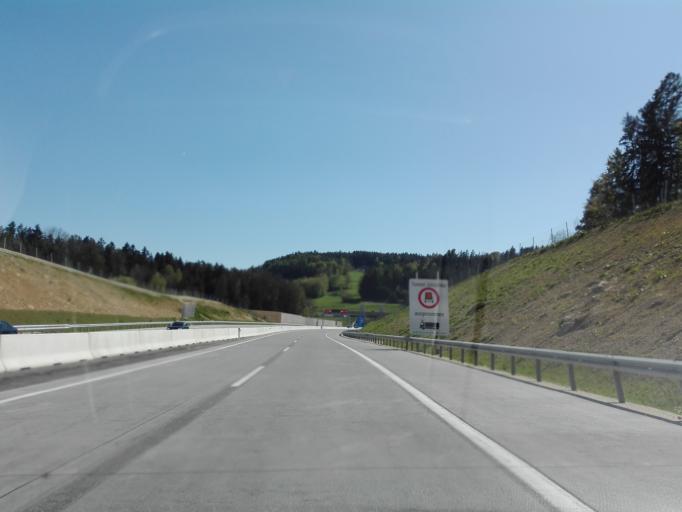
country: AT
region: Upper Austria
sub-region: Politischer Bezirk Urfahr-Umgebung
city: Alberndorf in der Riedmark
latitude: 48.4138
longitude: 14.4847
